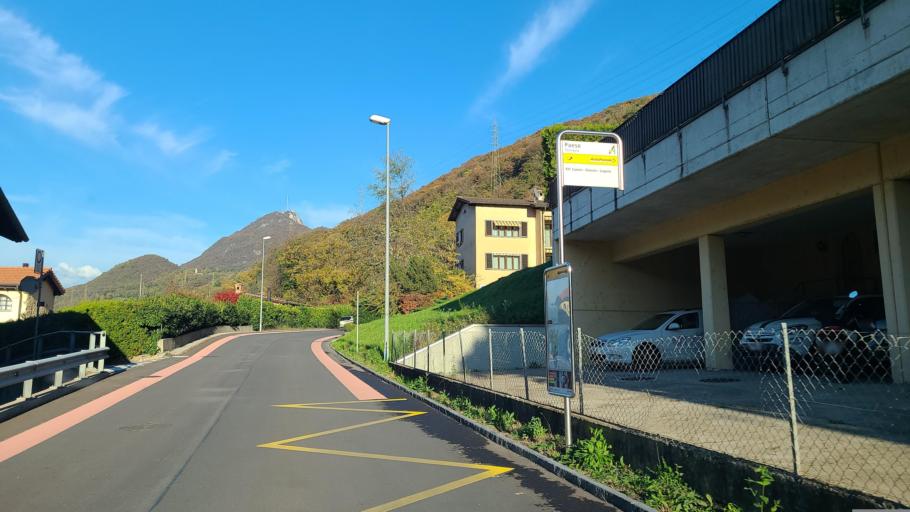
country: CH
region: Ticino
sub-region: Lugano District
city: Montagnola
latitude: 45.9558
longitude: 8.9196
